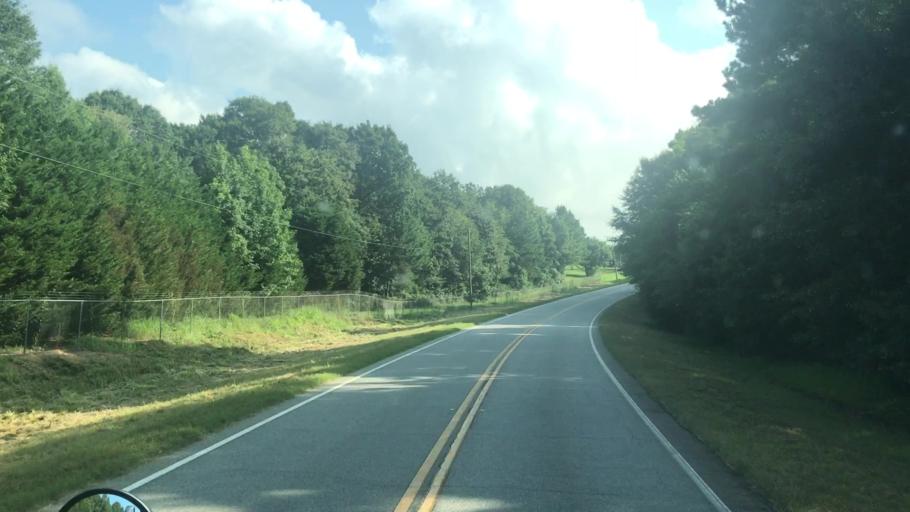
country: US
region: Florida
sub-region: Gadsden County
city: Havana
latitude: 30.7310
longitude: -84.4855
